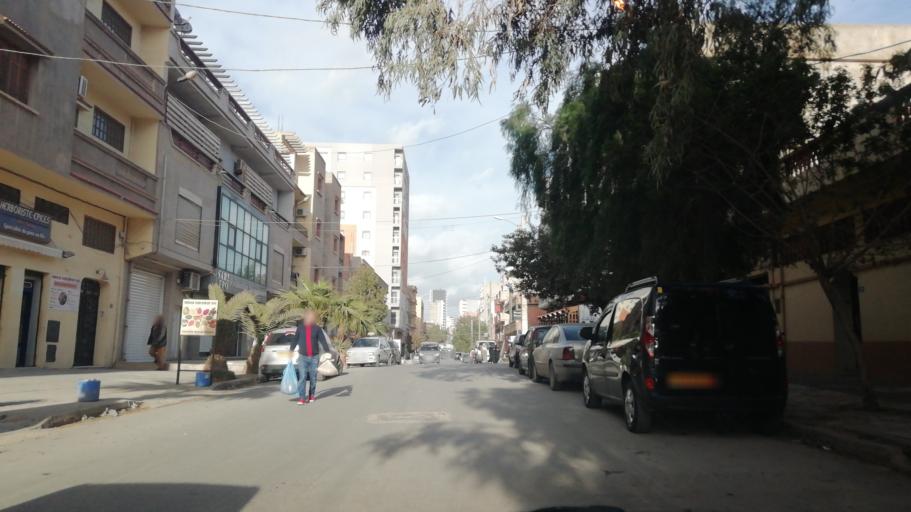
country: DZ
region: Oran
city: Bir el Djir
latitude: 35.7272
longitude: -0.5834
